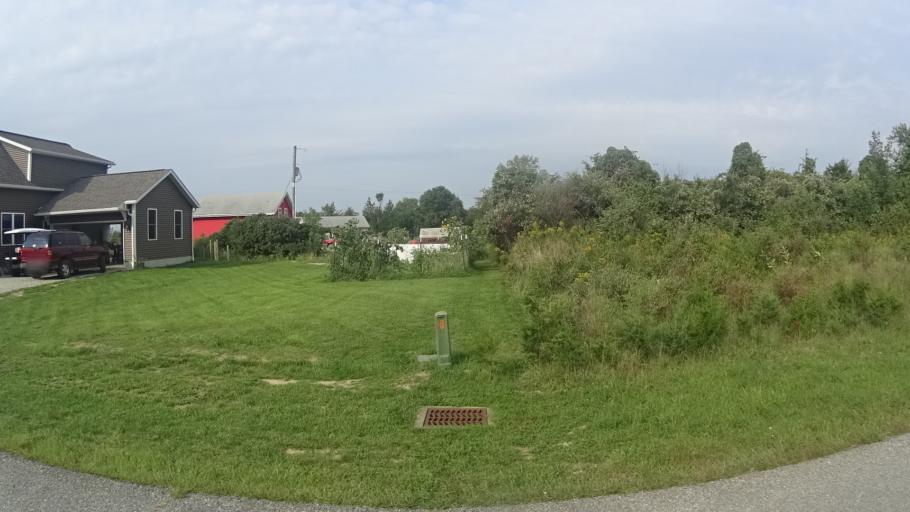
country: US
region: Ohio
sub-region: Erie County
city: Sandusky
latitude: 41.5940
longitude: -82.6961
